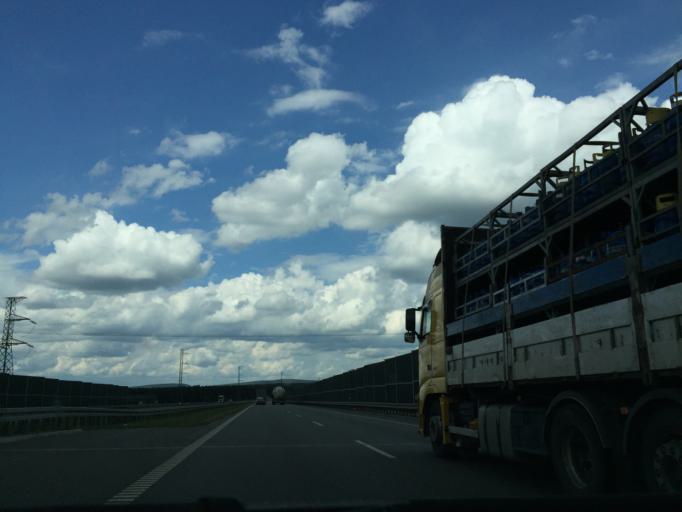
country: PL
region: Swietokrzyskie
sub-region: Powiat kielecki
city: Piekoszow
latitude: 50.8835
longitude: 20.5226
